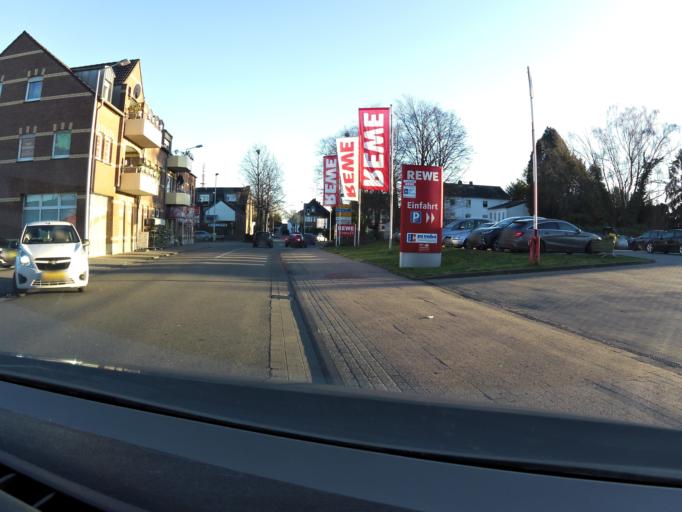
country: NL
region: Limburg
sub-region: Gemeente Venlo
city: Venlo
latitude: 51.3257
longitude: 6.2001
